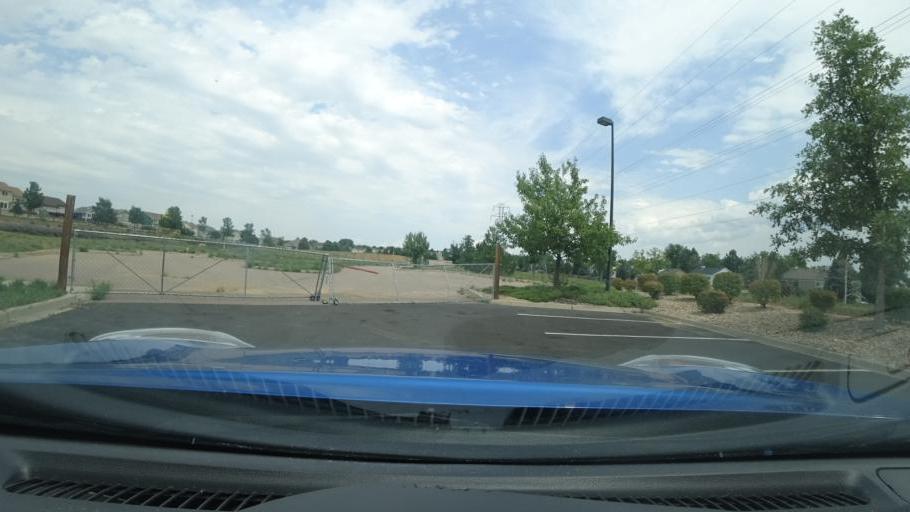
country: US
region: Colorado
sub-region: Adams County
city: Aurora
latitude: 39.6680
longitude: -104.7620
